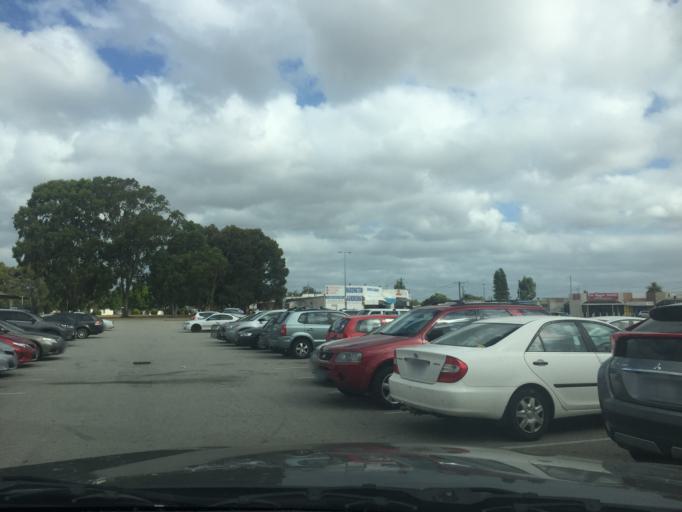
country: AU
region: Western Australia
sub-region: Gosnells
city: Maddington
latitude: -32.0533
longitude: 115.9793
